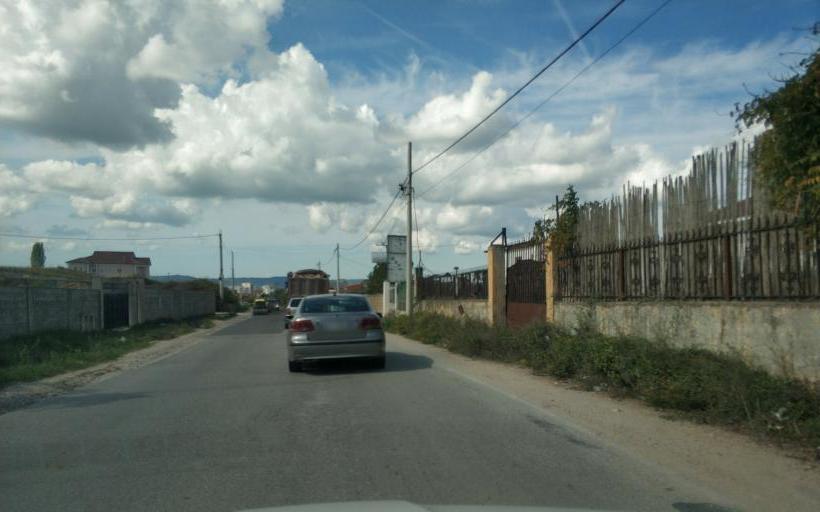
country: AL
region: Durres
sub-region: Rrethi i Krujes
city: Fushe-Kruje
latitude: 41.4777
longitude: 19.7410
